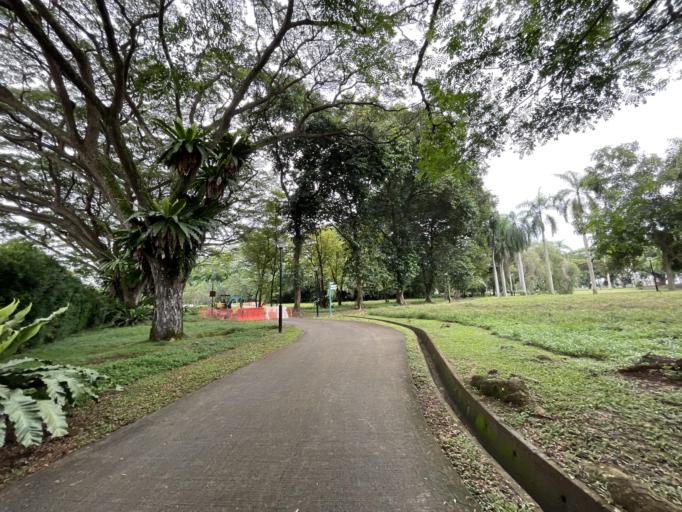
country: SG
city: Singapore
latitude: 1.2884
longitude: 103.7711
